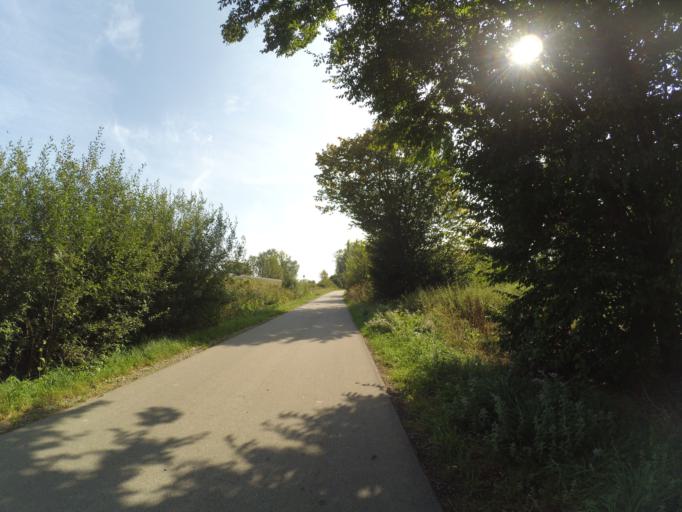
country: DE
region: Bavaria
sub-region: Swabia
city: Lamerdingen
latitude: 48.0825
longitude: 10.7302
